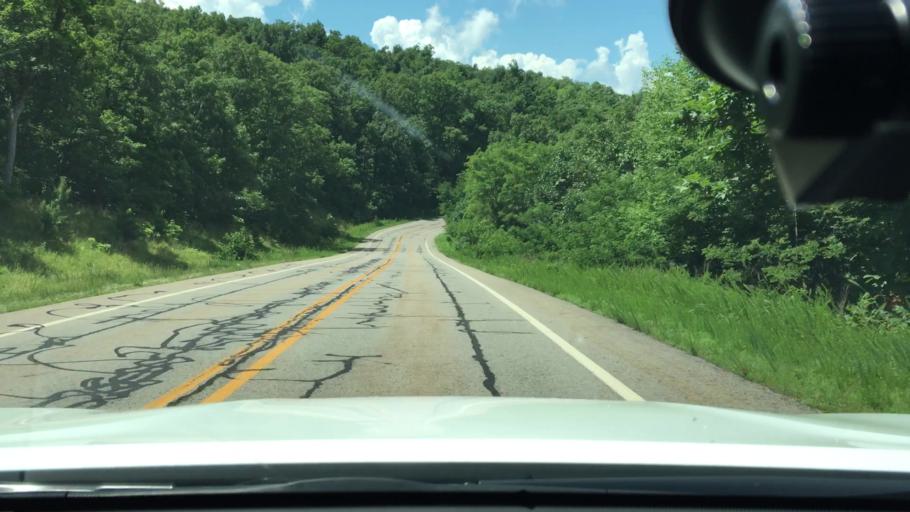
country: US
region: Arkansas
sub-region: Logan County
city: Paris
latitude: 35.1719
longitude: -93.6319
